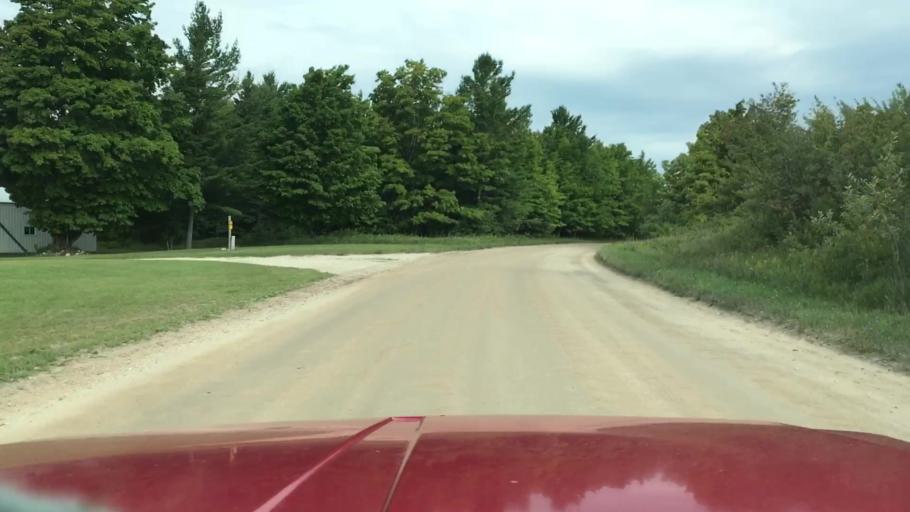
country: US
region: Michigan
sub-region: Charlevoix County
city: Charlevoix
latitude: 45.7209
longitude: -85.5154
